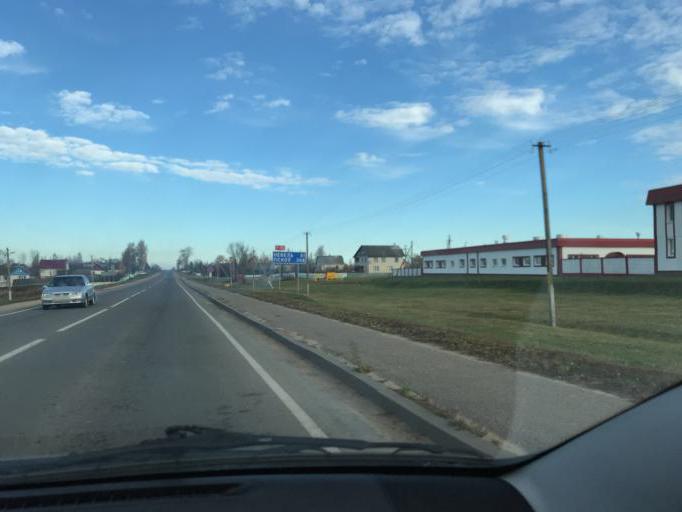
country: BY
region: Vitebsk
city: Haradok
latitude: 55.4734
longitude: 29.9695
